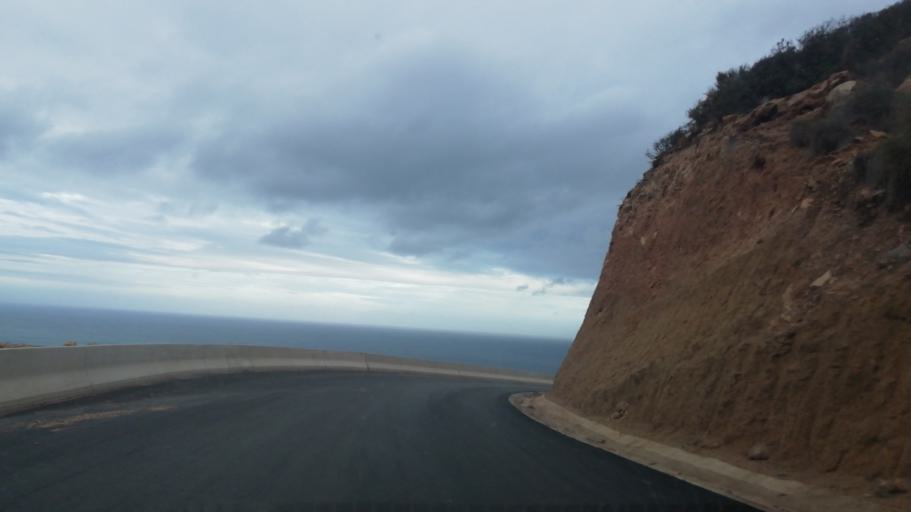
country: DZ
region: Oran
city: Bir el Djir
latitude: 35.7675
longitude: -0.5219
